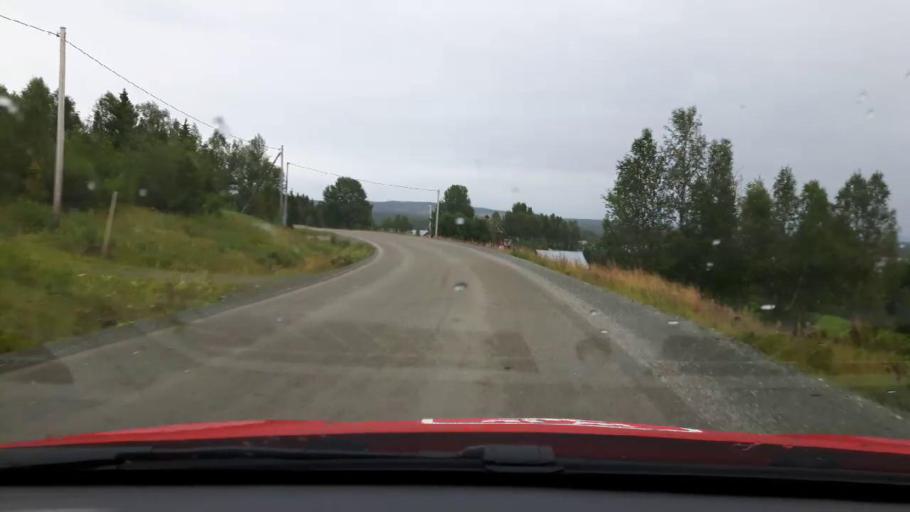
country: SE
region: Jaemtland
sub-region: Are Kommun
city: Are
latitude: 63.4599
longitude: 12.6363
